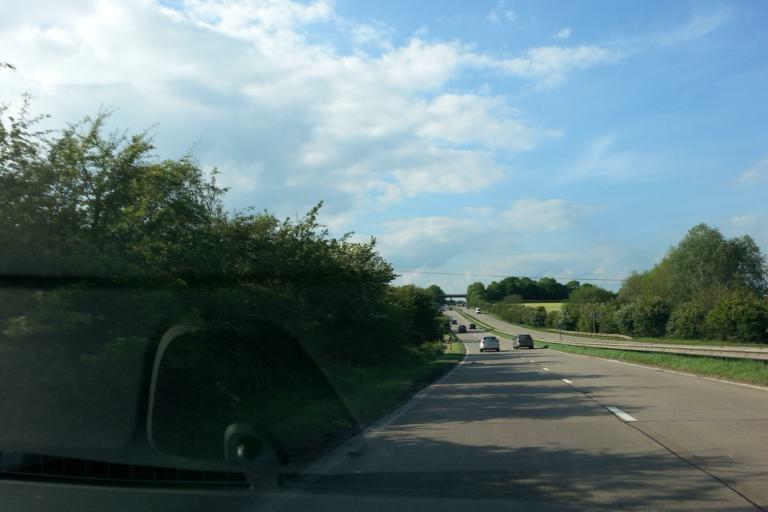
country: GB
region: England
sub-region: Leicestershire
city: Grimston
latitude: 52.8147
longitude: -1.0365
